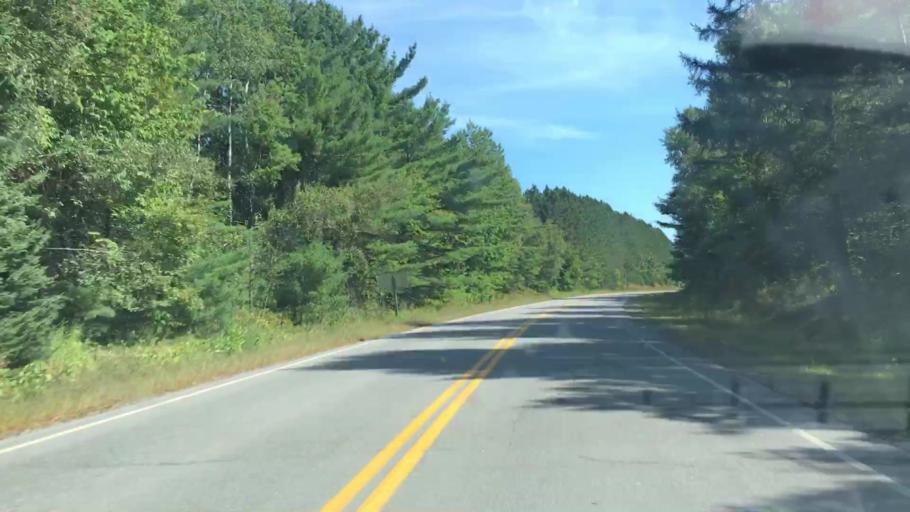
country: US
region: Maine
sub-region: Piscataquis County
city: Milo
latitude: 45.2296
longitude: -68.9355
